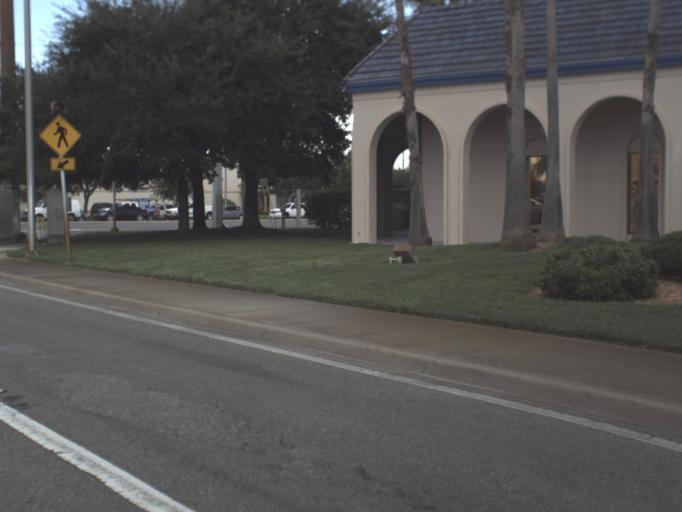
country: US
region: Florida
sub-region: Sarasota County
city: Gulf Gate Estates
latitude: 27.2600
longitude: -82.5221
